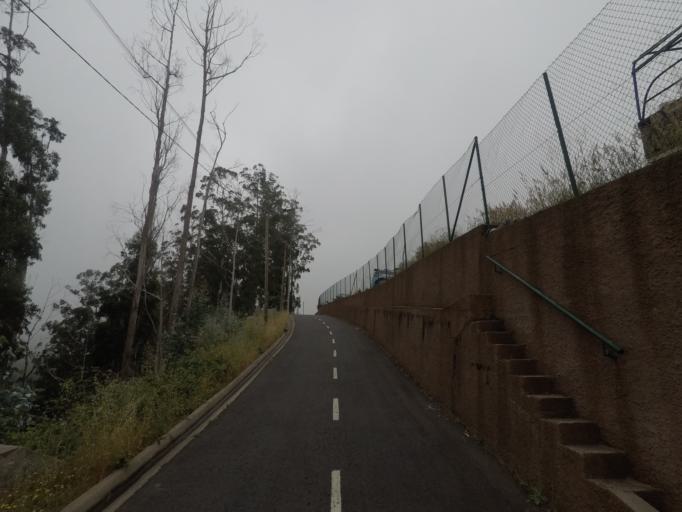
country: PT
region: Madeira
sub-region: Camara de Lobos
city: Curral das Freiras
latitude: 32.6873
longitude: -16.9479
